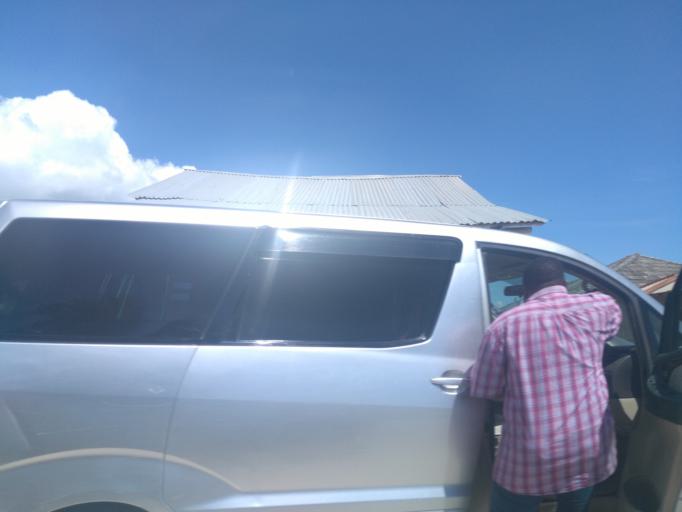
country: TZ
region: Zanzibar North
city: Gamba
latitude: -5.9247
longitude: 39.3552
